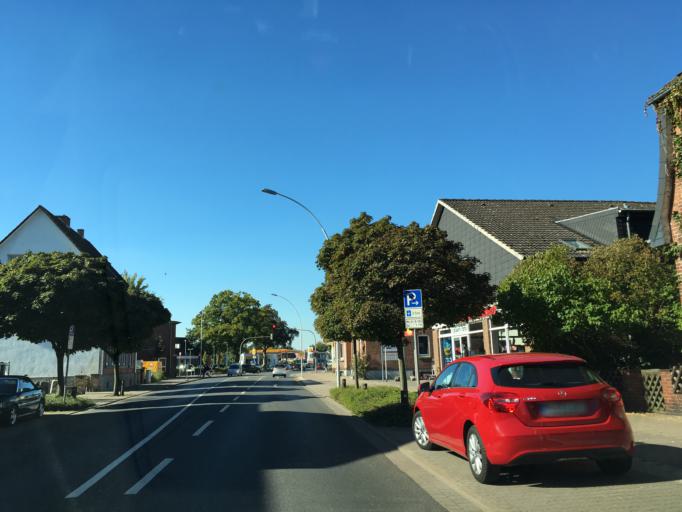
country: DE
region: Lower Saxony
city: Winsen
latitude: 53.3558
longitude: 10.2077
